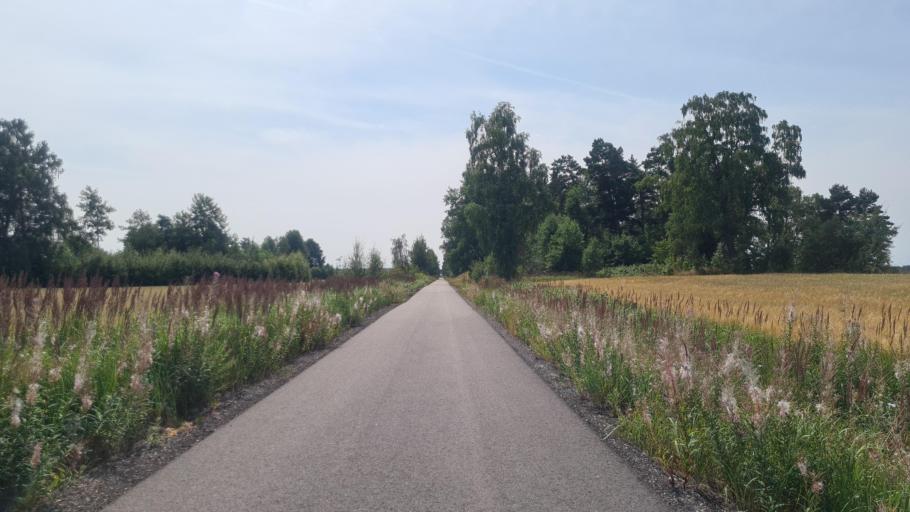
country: SE
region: Kronoberg
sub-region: Ljungby Kommun
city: Lagan
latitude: 56.8922
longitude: 13.9849
